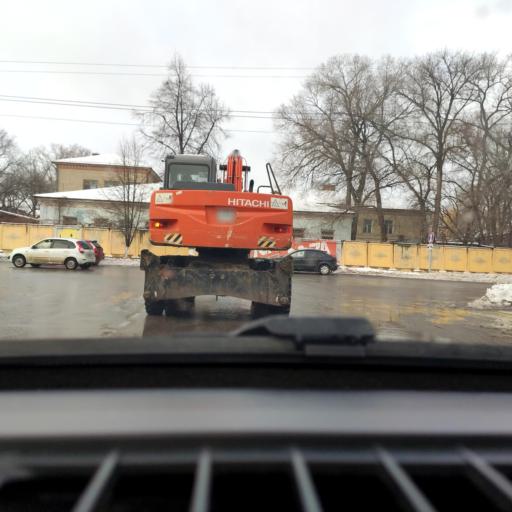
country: RU
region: Voronezj
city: Semiluki
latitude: 51.6844
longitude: 39.0339
